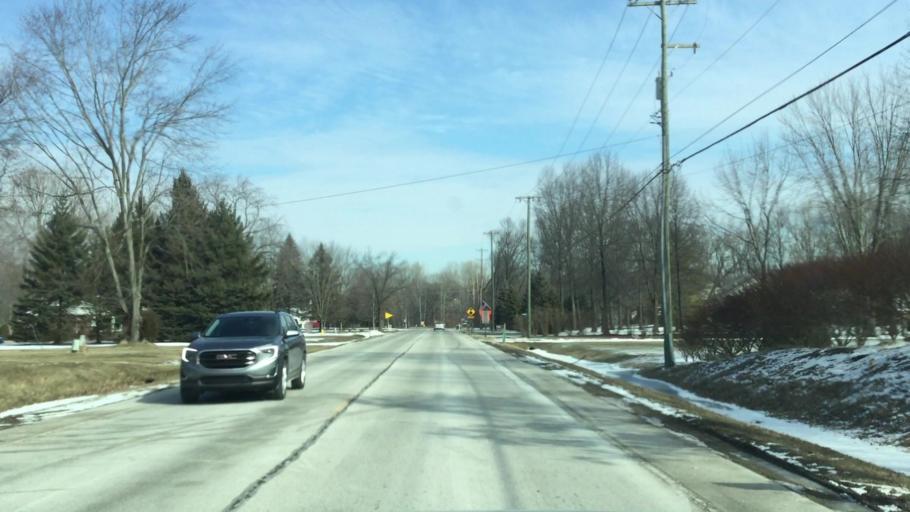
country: US
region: Michigan
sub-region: Wayne County
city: Flat Rock
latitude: 42.1351
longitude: -83.2900
